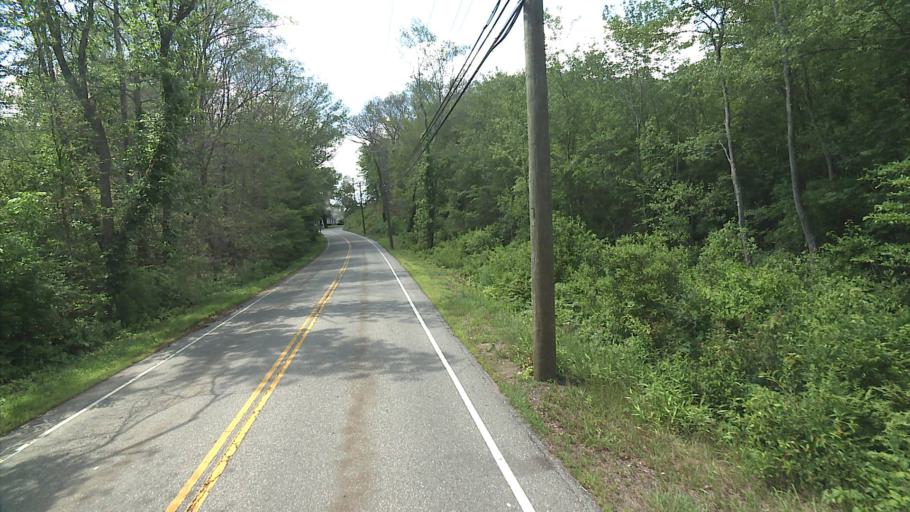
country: US
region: Connecticut
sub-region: Middlesex County
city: Moodus
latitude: 41.5026
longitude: -72.4722
